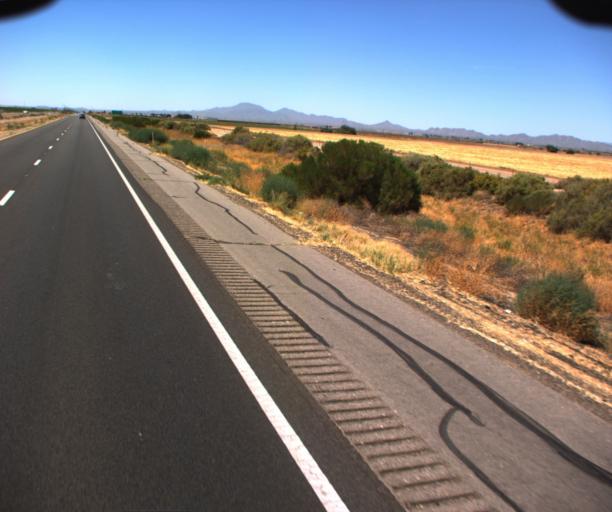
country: US
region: Arizona
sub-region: Pinal County
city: Maricopa
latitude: 33.0036
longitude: -112.0481
